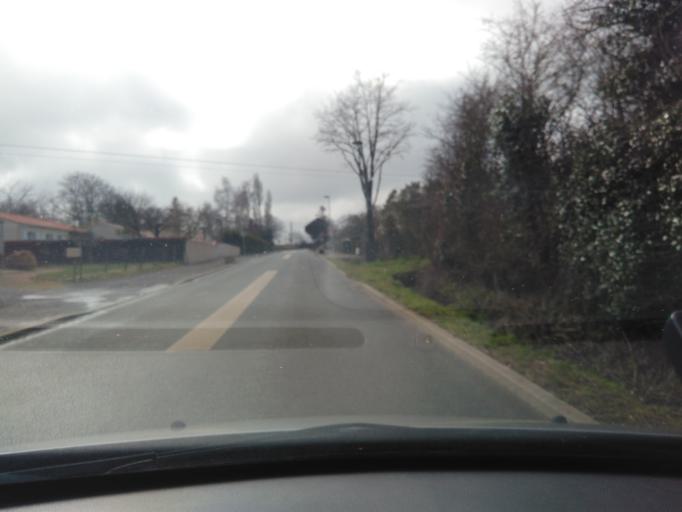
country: FR
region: Pays de la Loire
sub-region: Departement de la Vendee
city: Sainte-Cecile
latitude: 46.6925
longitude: -1.1299
